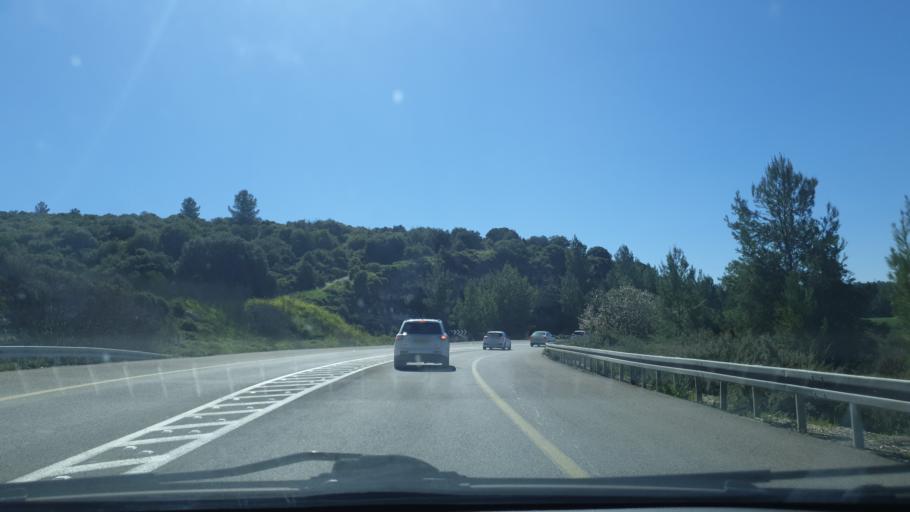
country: IL
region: Jerusalem
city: Bet Shemesh
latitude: 31.6952
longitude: 34.9433
